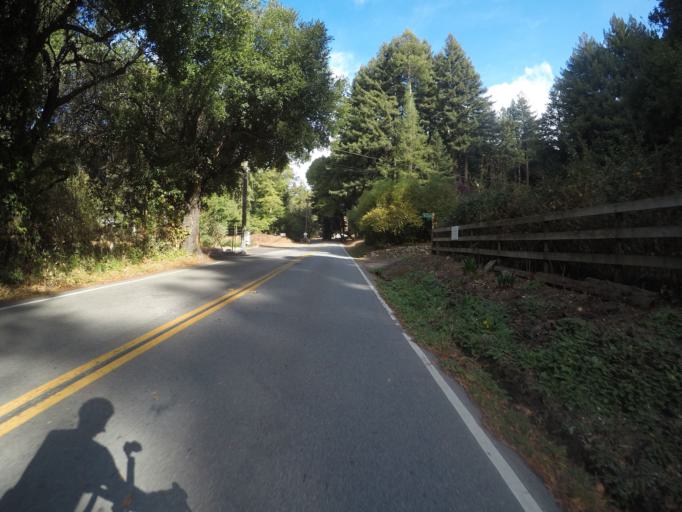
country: US
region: California
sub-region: Santa Cruz County
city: Scotts Valley
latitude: 37.0518
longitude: -121.9788
